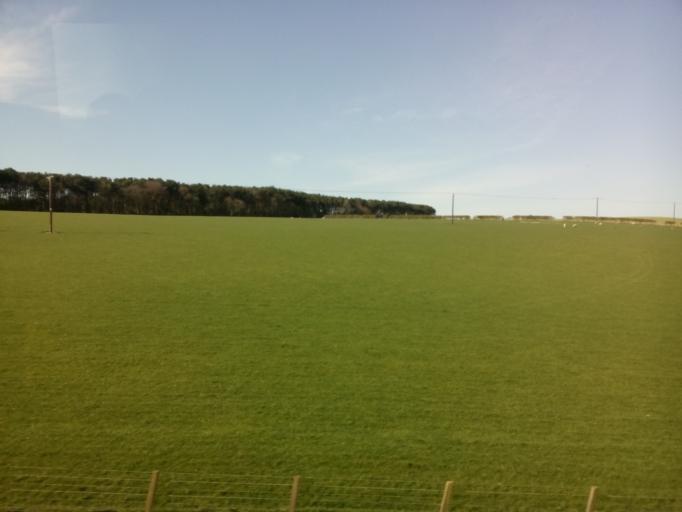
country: GB
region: Scotland
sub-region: The Scottish Borders
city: Chirnside
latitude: 55.8372
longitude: -2.1608
